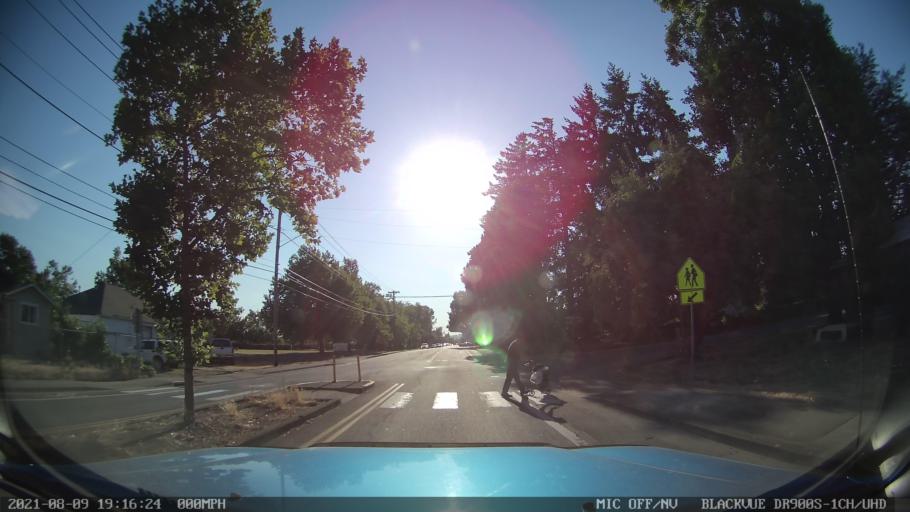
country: US
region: Oregon
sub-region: Marion County
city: Four Corners
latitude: 44.9399
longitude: -122.9947
